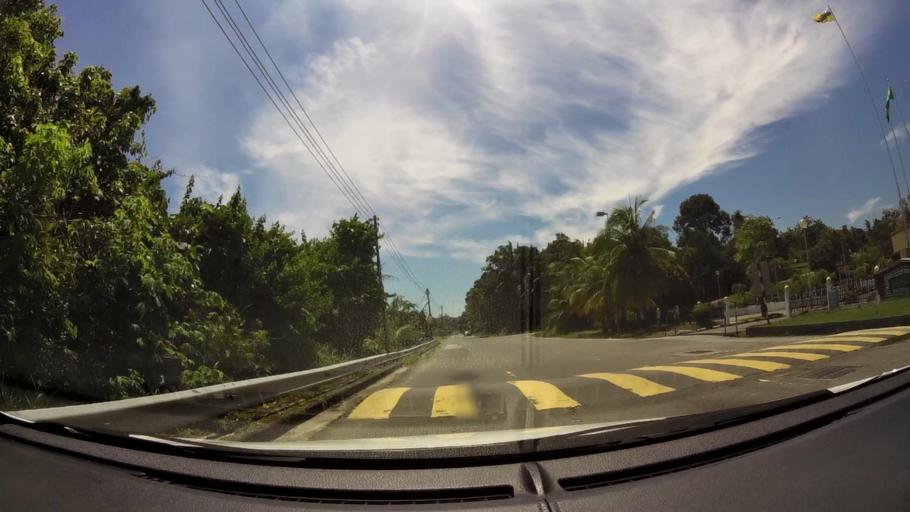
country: BN
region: Brunei and Muara
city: Bandar Seri Begawan
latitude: 4.9338
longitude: 114.9516
